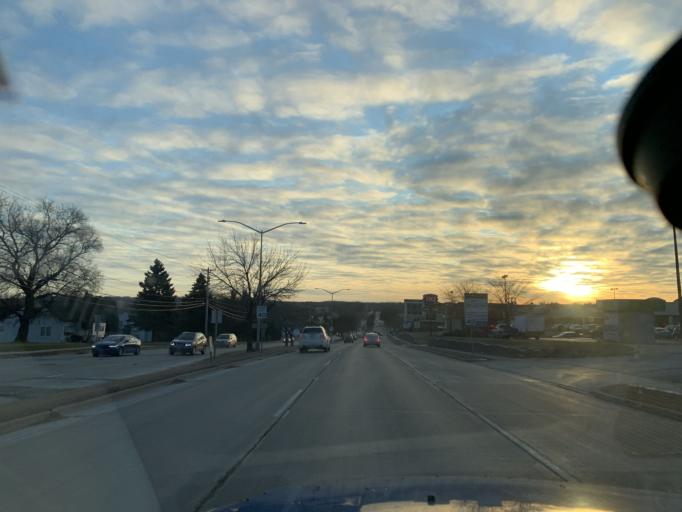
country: US
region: Wisconsin
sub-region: Dane County
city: Madison
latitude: 43.0261
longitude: -89.4132
